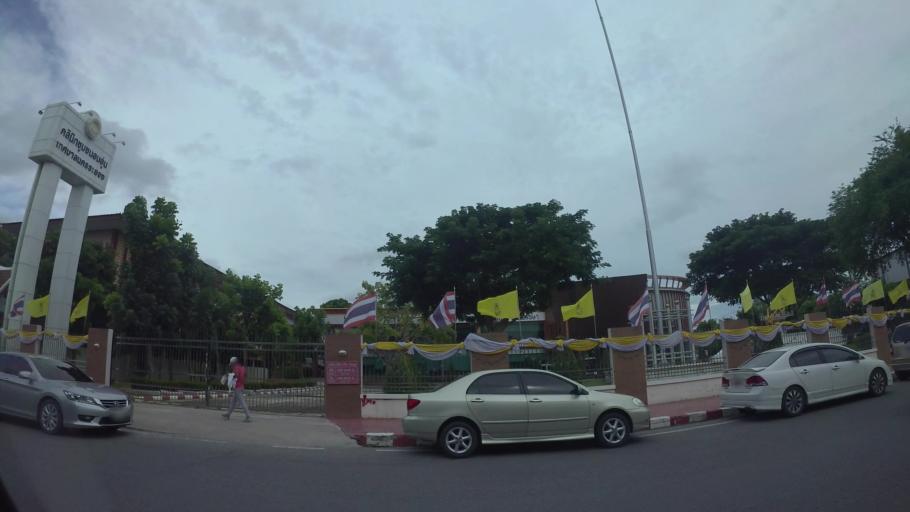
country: TH
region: Rayong
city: Rayong
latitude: 12.6746
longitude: 101.2783
